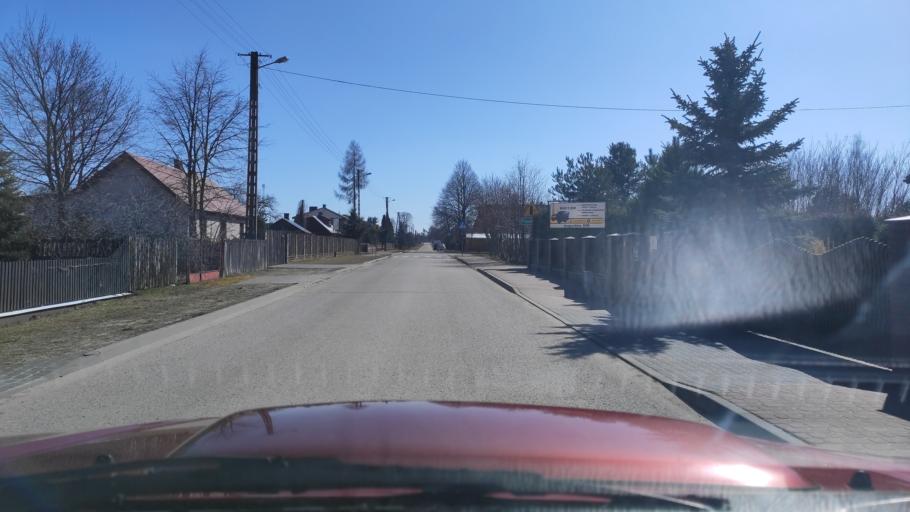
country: PL
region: Masovian Voivodeship
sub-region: Powiat radomski
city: Pionki
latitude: 51.5223
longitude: 21.4719
